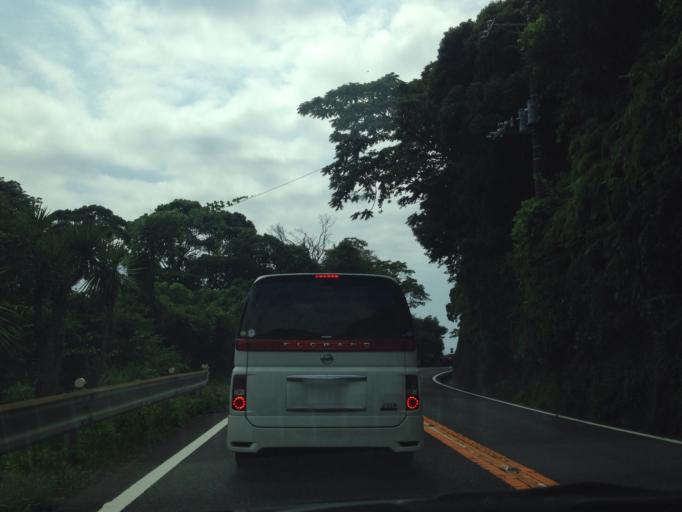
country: JP
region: Shizuoka
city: Shimoda
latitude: 34.7264
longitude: 138.9904
